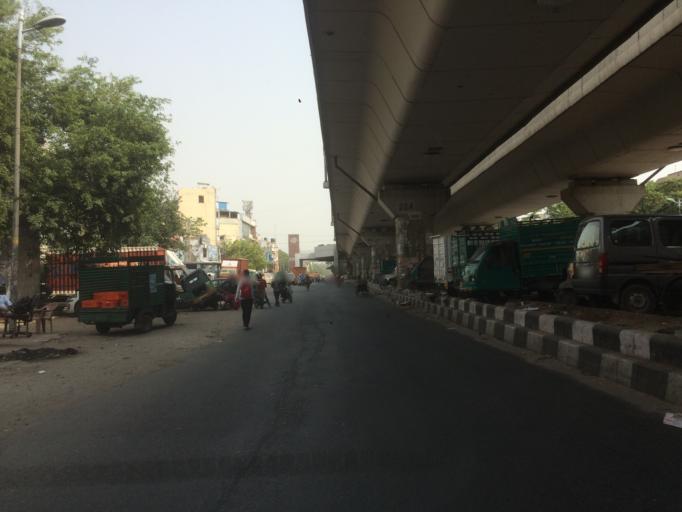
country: IN
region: NCT
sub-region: Central Delhi
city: Karol Bagh
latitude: 28.6241
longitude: 77.1349
